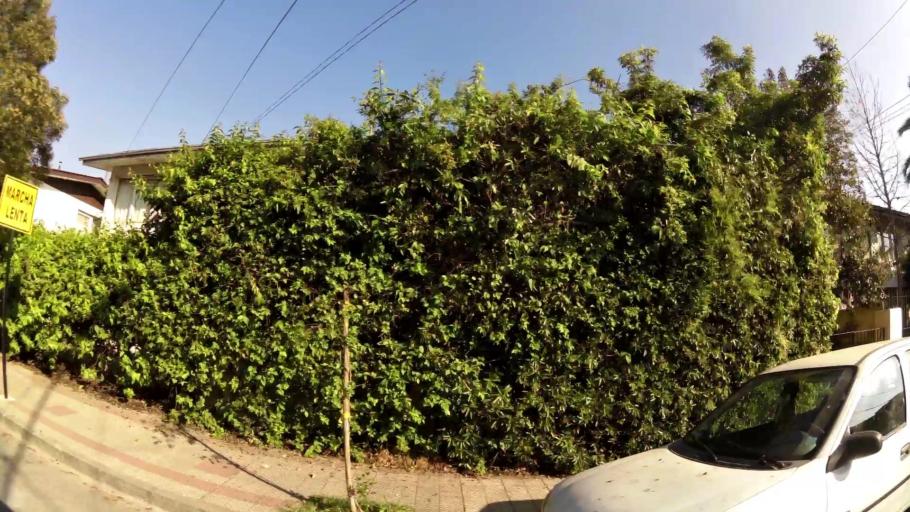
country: CL
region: Santiago Metropolitan
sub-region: Provincia de Santiago
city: Villa Presidente Frei, Nunoa, Santiago, Chile
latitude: -33.4448
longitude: -70.6079
